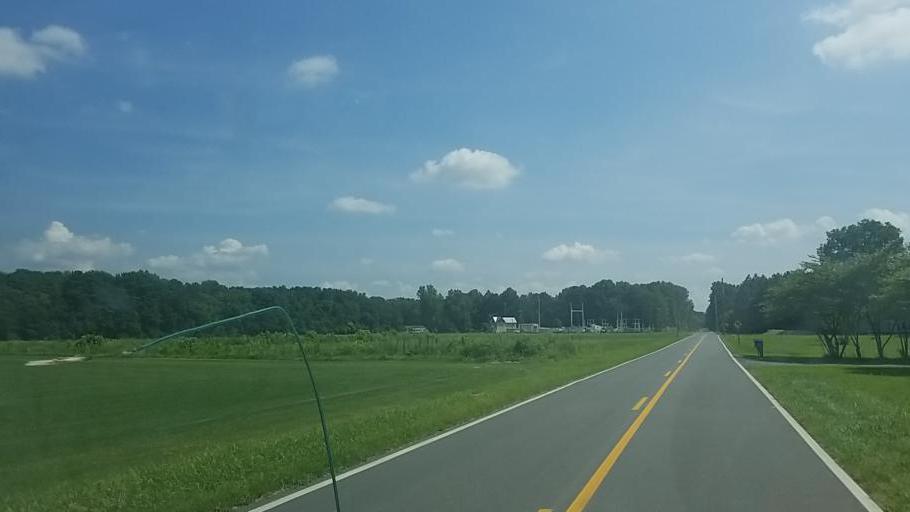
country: US
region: Maryland
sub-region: Wicomico County
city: Hebron
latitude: 38.4272
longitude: -75.6977
